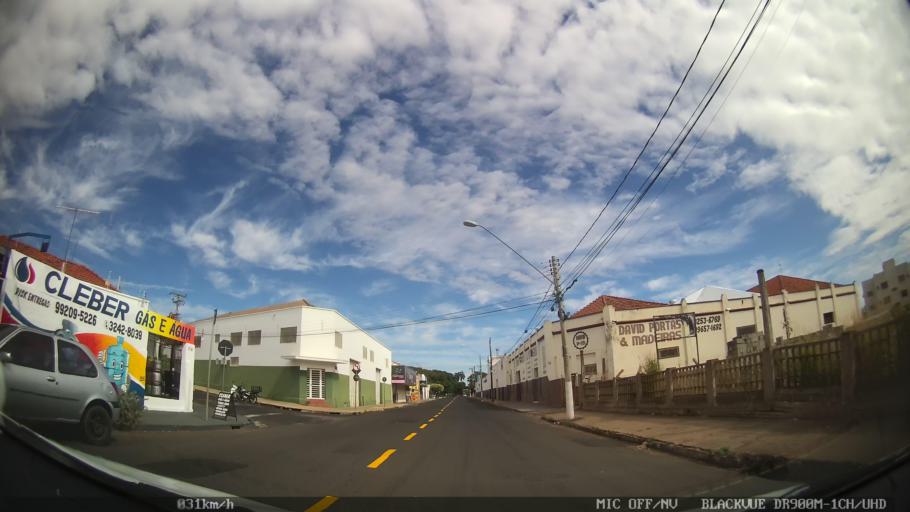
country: BR
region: Sao Paulo
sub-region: Bady Bassitt
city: Bady Bassitt
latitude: -20.8145
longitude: -49.5161
